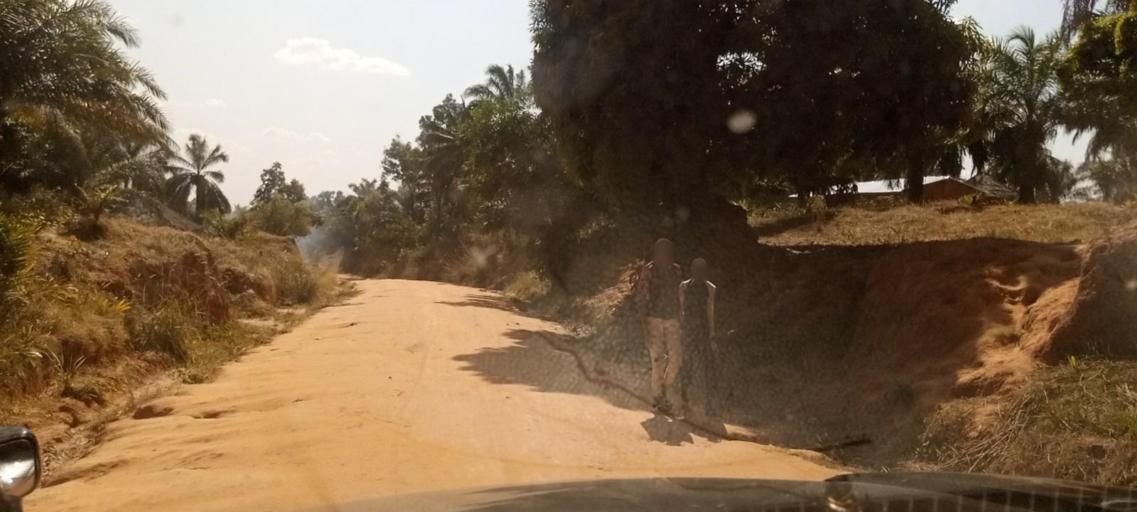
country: CD
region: Kasai-Oriental
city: Kabinda
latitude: -6.1299
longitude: 24.5224
